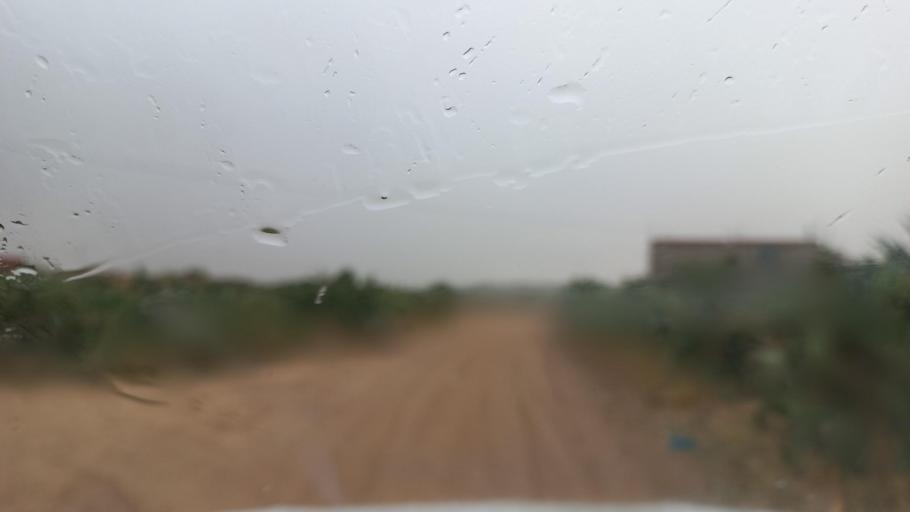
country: TN
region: Al Qasrayn
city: Kasserine
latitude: 35.2742
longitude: 8.9405
